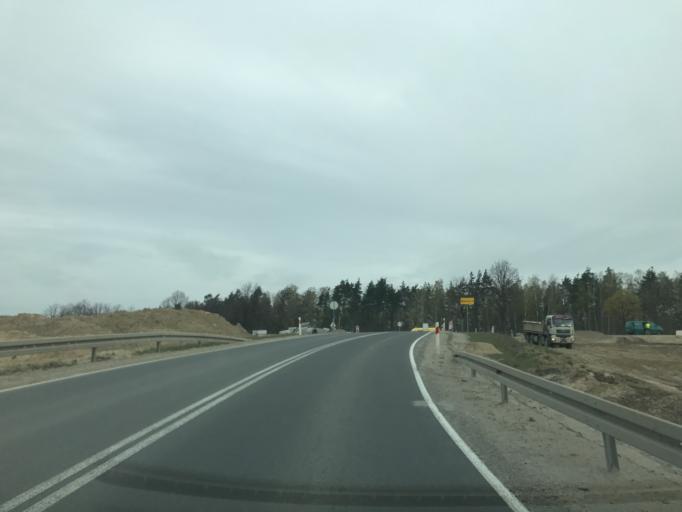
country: PL
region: Warmian-Masurian Voivodeship
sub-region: Powiat ostrodzki
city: Gierzwald
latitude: 53.6010
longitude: 20.0781
